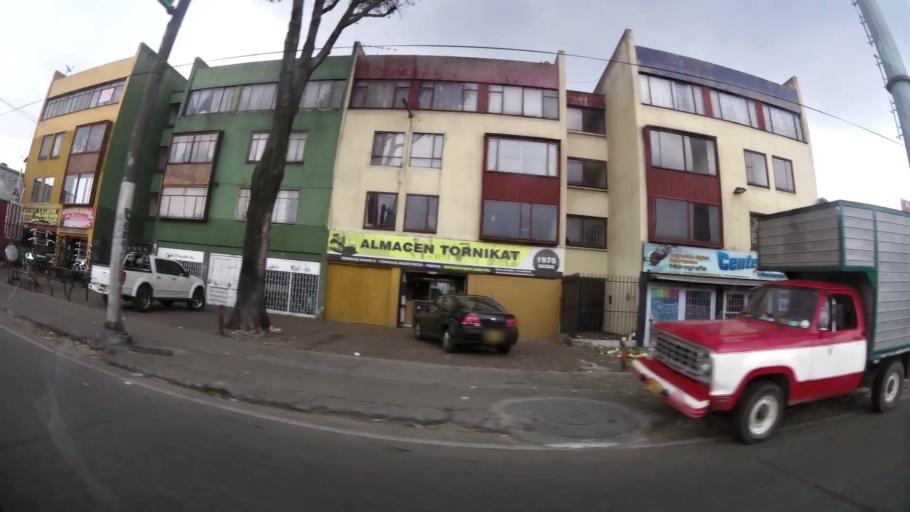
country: CO
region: Bogota D.C.
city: Bogota
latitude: 4.6000
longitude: -74.0887
